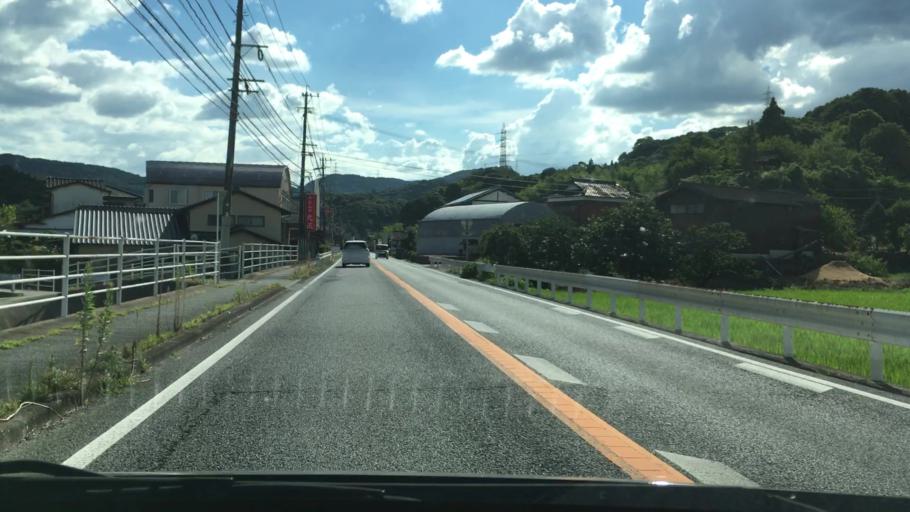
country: JP
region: Saga Prefecture
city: Takeocho-takeo
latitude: 33.1863
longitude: 130.0001
